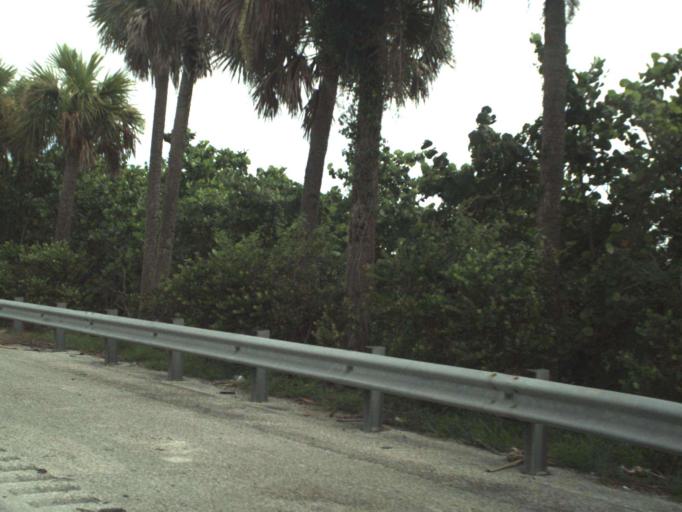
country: US
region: Florida
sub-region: Martin County
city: Palm City
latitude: 27.1175
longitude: -80.2669
